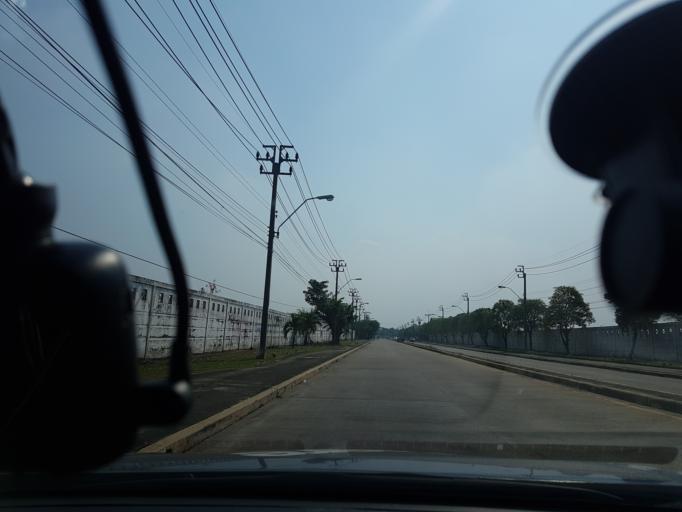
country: TH
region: Bangkok
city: Khan Na Yao
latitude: 13.8496
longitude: 100.6997
